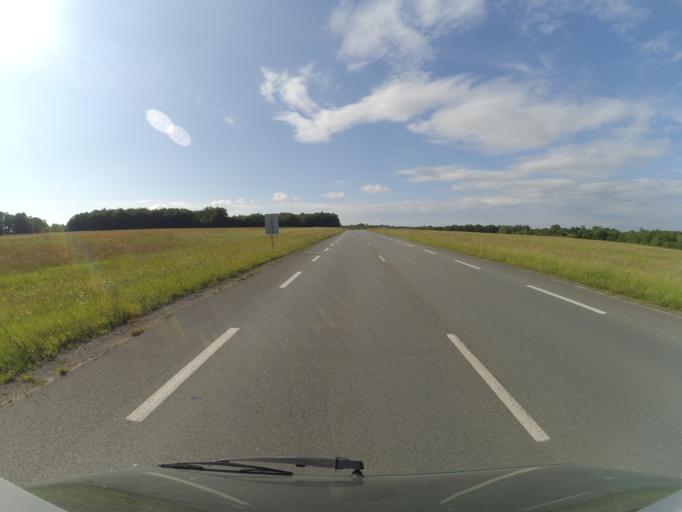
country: FR
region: Poitou-Charentes
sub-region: Departement de la Charente-Maritime
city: Saint-Agnant
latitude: 45.8306
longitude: -0.9372
